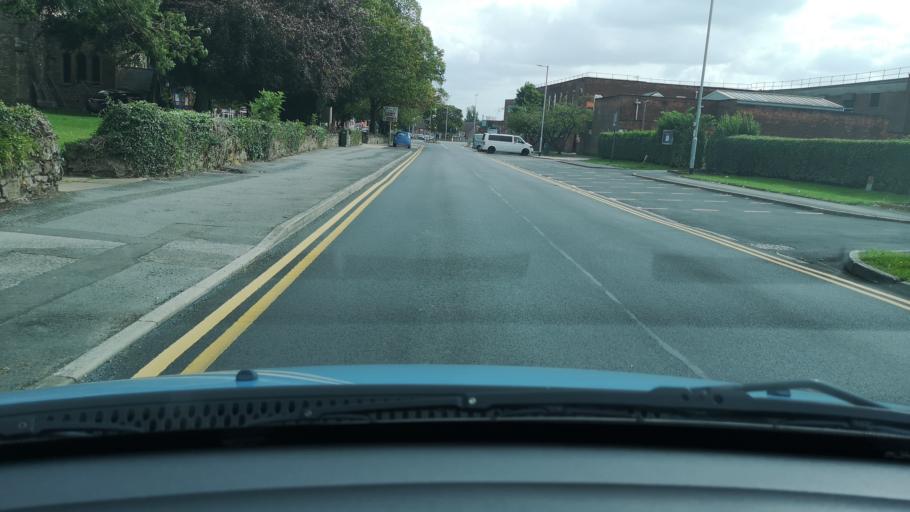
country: GB
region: England
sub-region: North Lincolnshire
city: Scunthorpe
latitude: 53.5863
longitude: -0.6564
